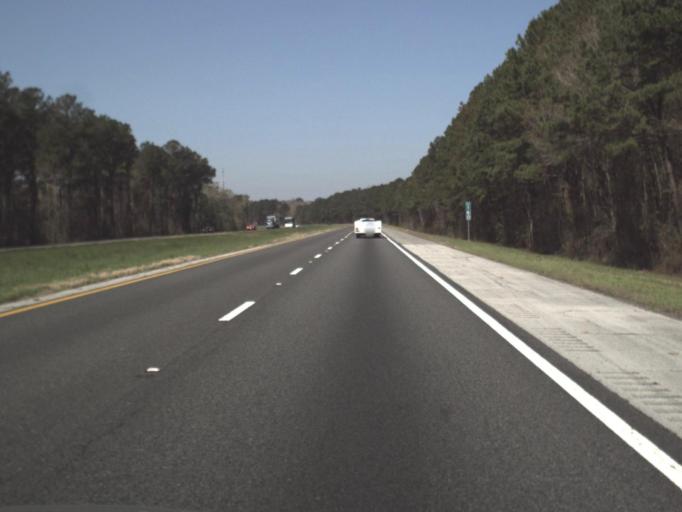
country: US
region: Florida
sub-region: Jackson County
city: Sneads
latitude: 30.6369
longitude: -84.9123
